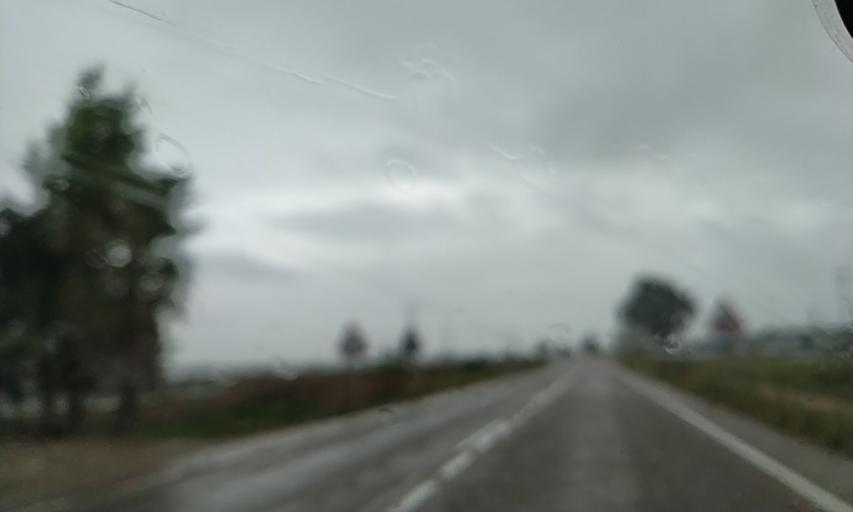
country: ES
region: Extremadura
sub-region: Provincia de Badajoz
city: Badajoz
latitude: 38.9265
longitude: -6.9363
